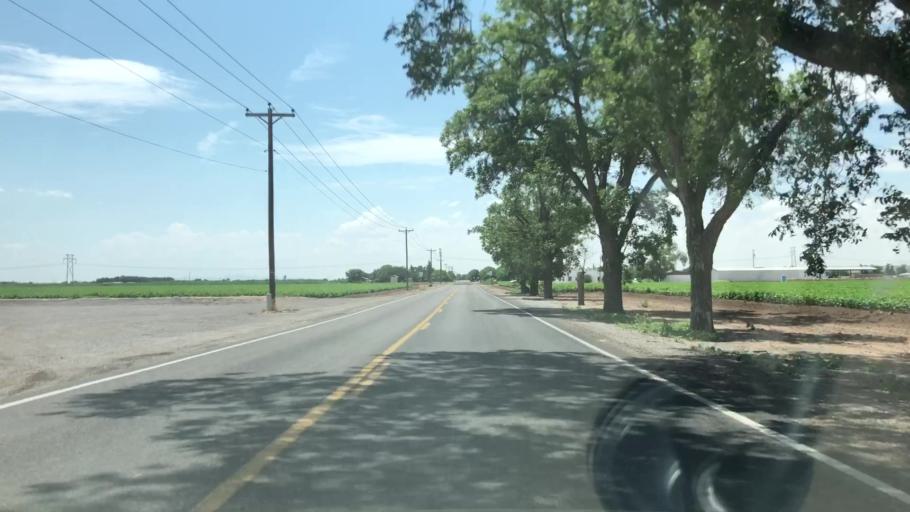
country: US
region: New Mexico
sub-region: Dona Ana County
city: Vado
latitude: 32.1026
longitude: -106.6836
